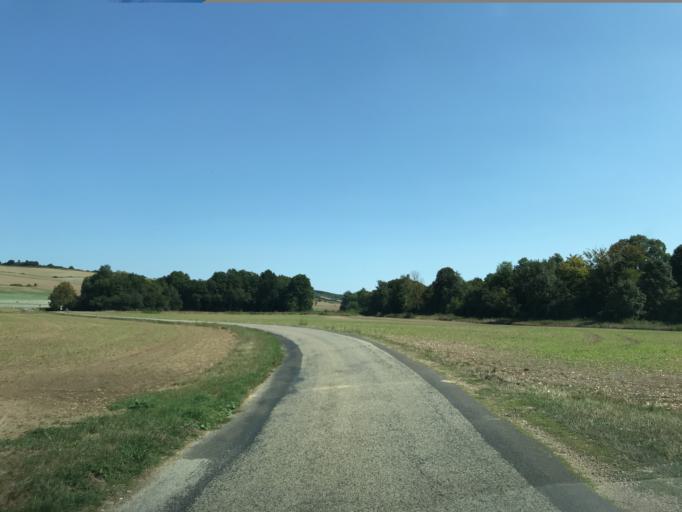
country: FR
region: Haute-Normandie
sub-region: Departement de l'Eure
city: Heudreville-sur-Eure
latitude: 49.1178
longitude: 1.2181
